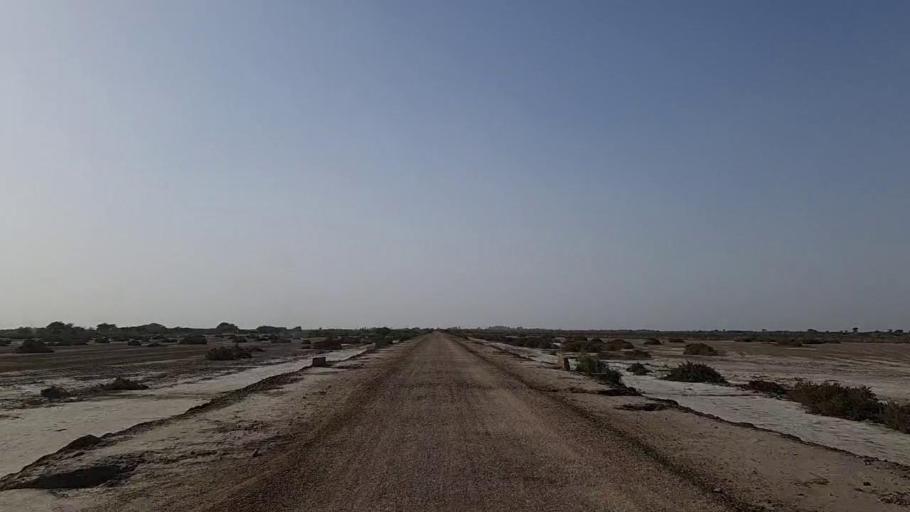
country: PK
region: Sindh
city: Jati
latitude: 24.2809
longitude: 68.2278
